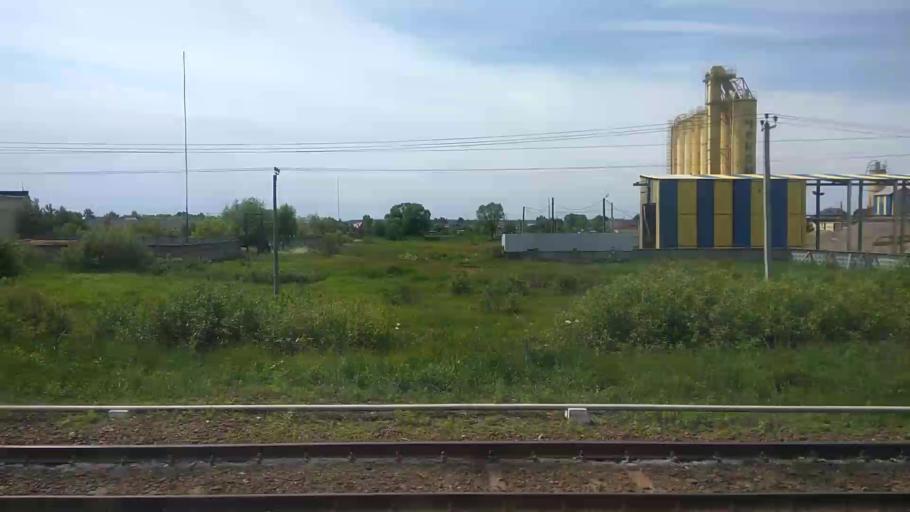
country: RU
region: Moskovskaya
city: Malyshevo
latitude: 55.5043
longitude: 38.3536
